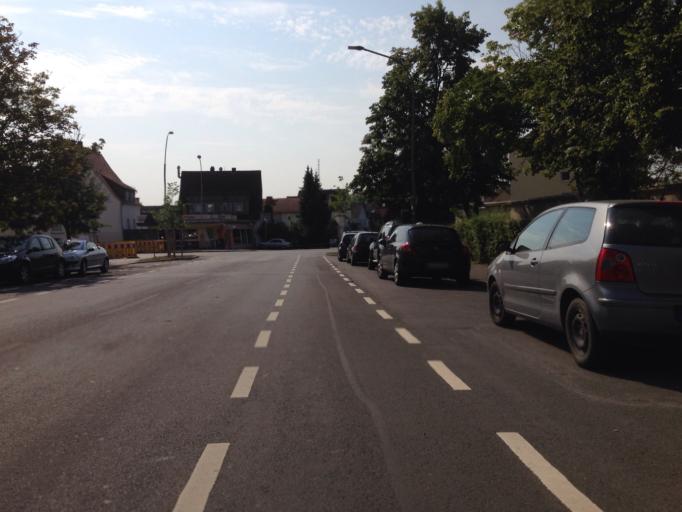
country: DE
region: Hesse
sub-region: Regierungsbezirk Giessen
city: Giessen
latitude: 50.6005
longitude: 8.6959
